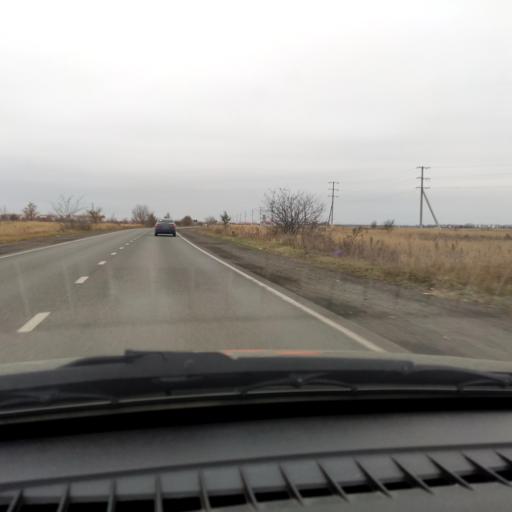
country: RU
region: Samara
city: Podstepki
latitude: 53.5191
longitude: 49.2070
